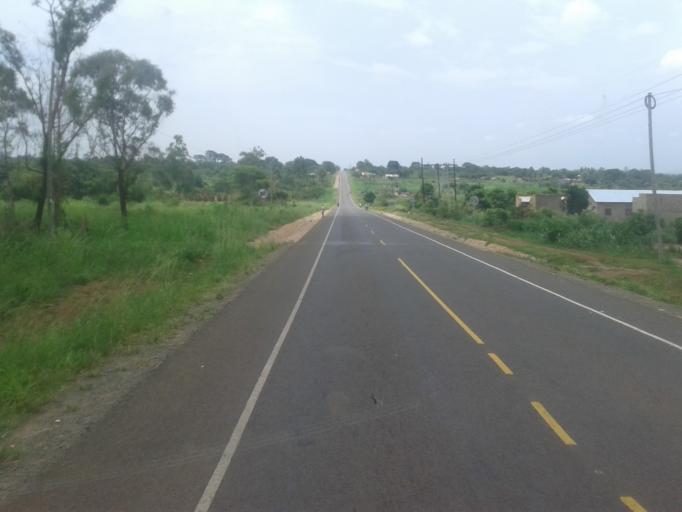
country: UG
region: Western Region
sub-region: Kiryandongo District
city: Kiryandongo
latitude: 1.8804
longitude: 32.0643
